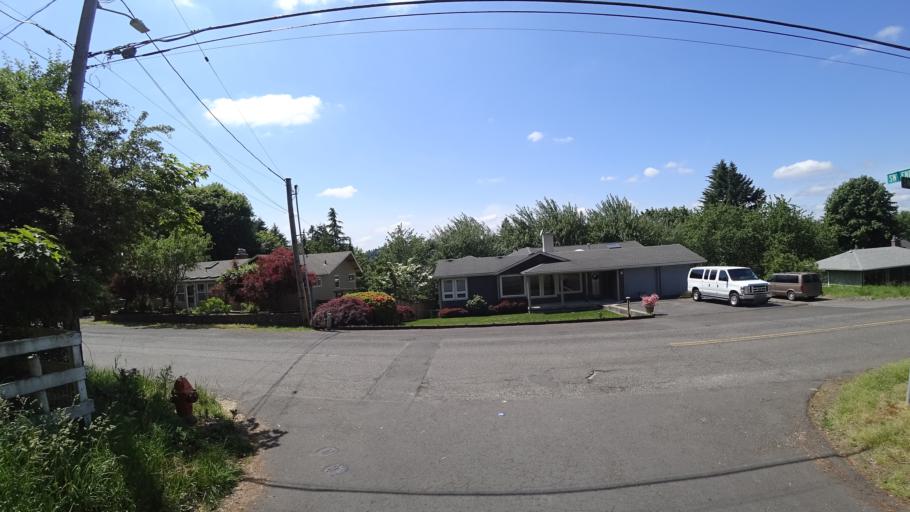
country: US
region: Oregon
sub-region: Clackamas County
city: Lake Oswego
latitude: 45.4338
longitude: -122.6972
